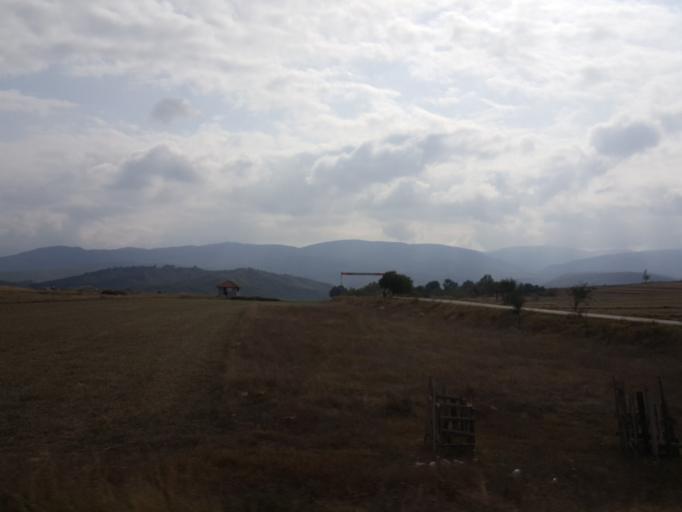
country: TR
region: Sinop
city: Sarayduzu
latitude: 41.3433
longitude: 34.8119
